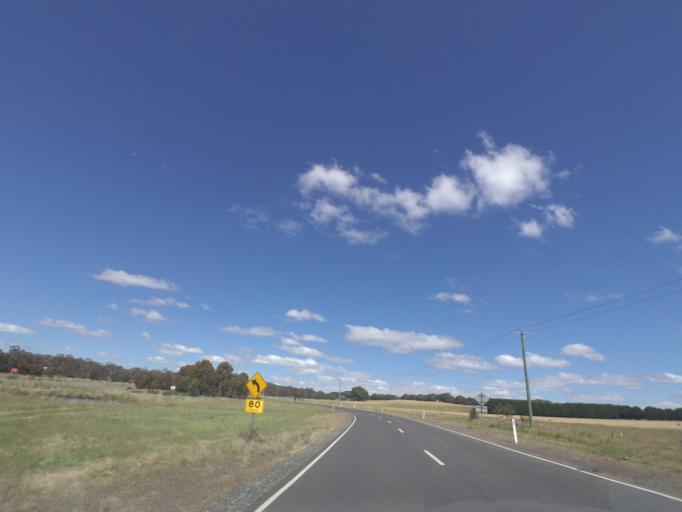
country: AU
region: Victoria
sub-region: Hume
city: Sunbury
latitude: -37.2967
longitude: 144.5006
